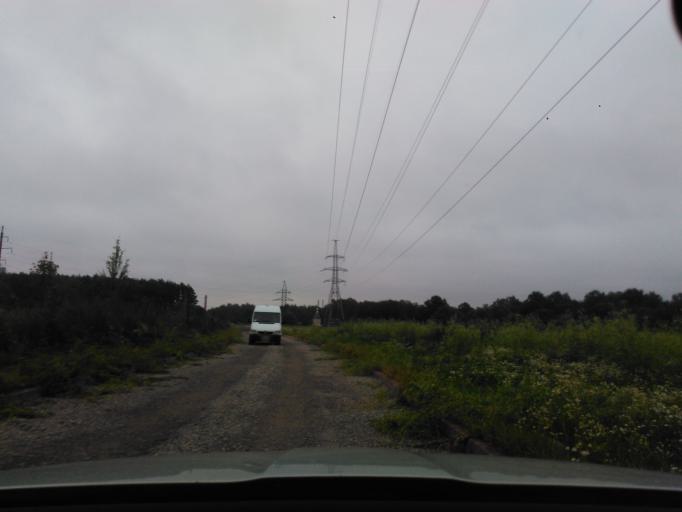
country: RU
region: Moskovskaya
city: Firsanovka
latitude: 55.9391
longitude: 37.2441
